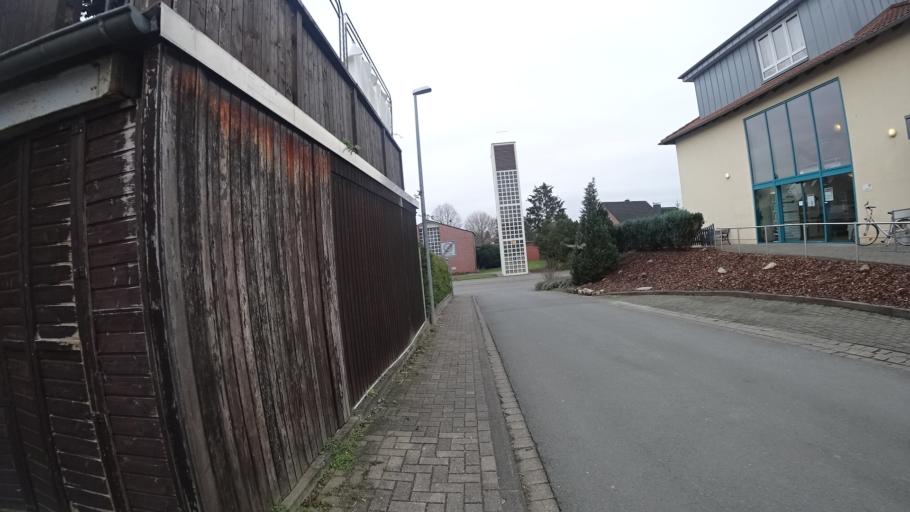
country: DE
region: Lower Saxony
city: Lauenau
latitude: 52.2756
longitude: 9.3721
